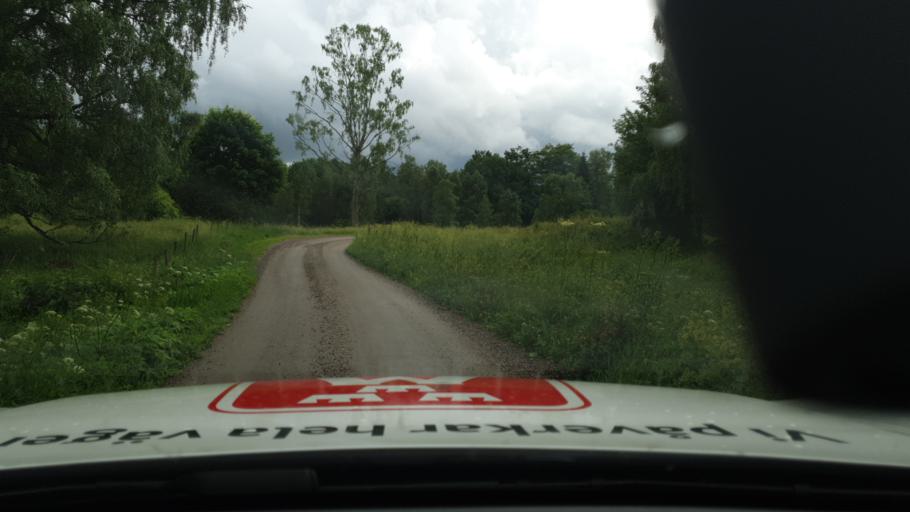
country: SE
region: Vaestra Goetaland
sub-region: Falkopings Kommun
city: Falkoeping
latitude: 58.0594
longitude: 13.6610
